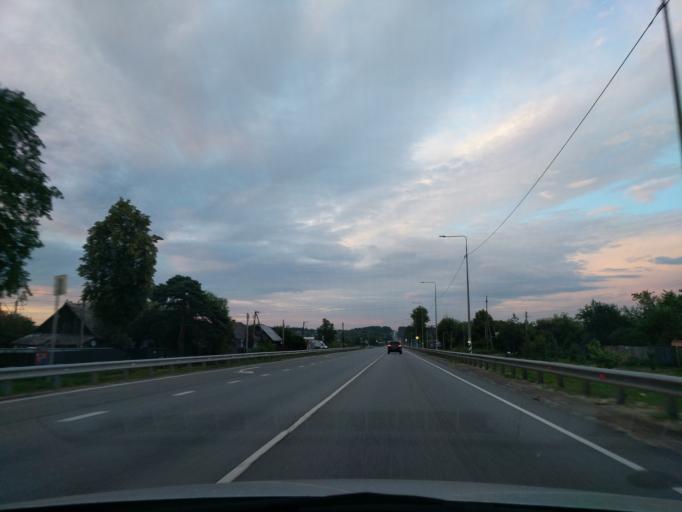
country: RU
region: Kaluga
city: Obninsk
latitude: 55.0536
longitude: 36.5697
